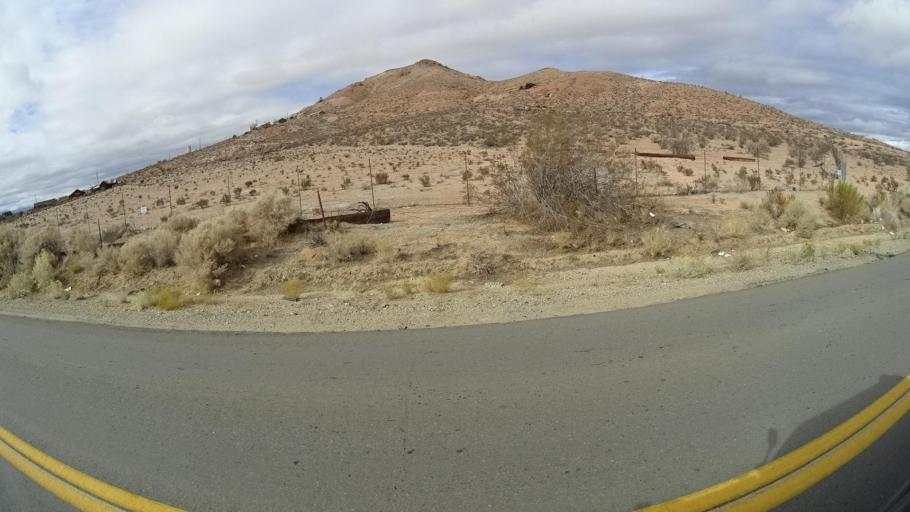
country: US
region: California
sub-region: Kern County
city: Rosamond
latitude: 34.8762
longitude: -118.2266
